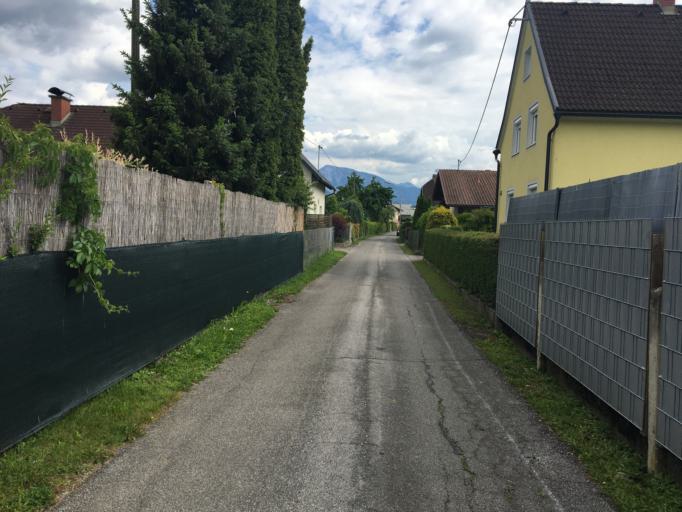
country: AT
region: Carinthia
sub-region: Klagenfurt am Woerthersee
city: Klagenfurt am Woerthersee
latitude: 46.5986
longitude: 14.2725
